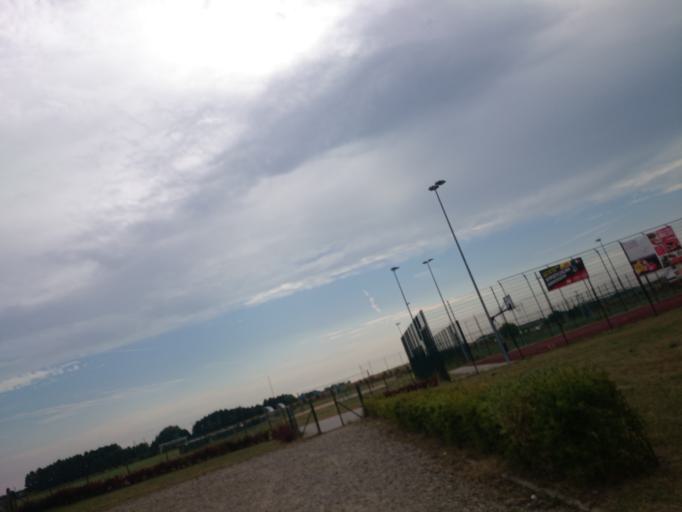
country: PL
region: West Pomeranian Voivodeship
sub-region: Powiat gryfinski
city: Moryn
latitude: 52.8542
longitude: 14.3942
